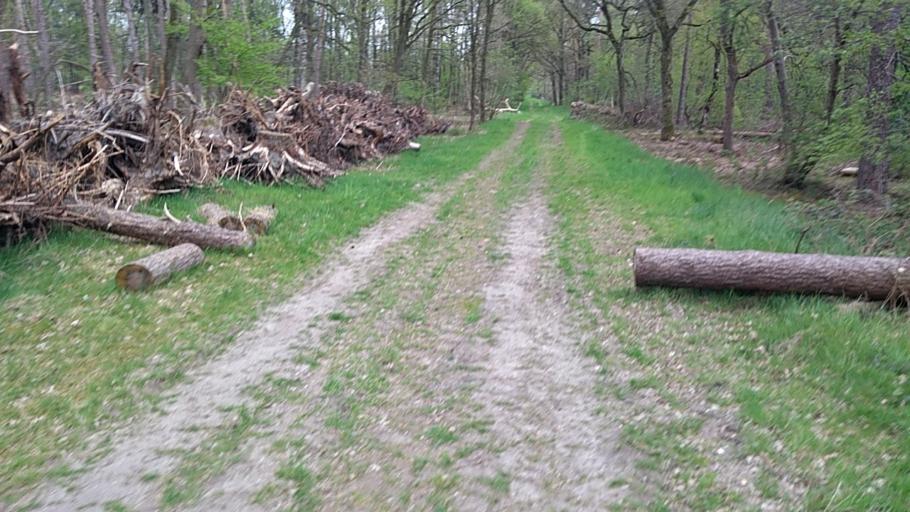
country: NL
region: Limburg
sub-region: Gemeente Leudal
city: Heythuysen
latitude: 51.2946
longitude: 5.8651
